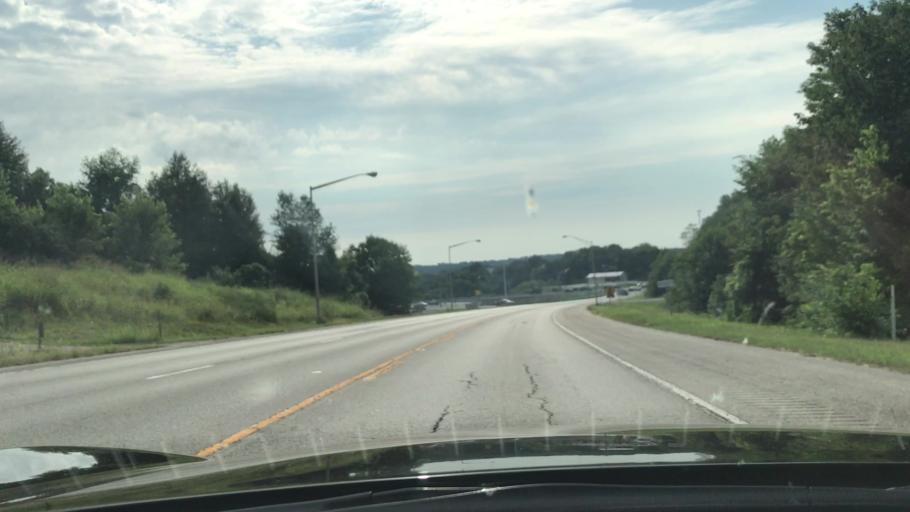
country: US
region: Kentucky
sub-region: Green County
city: Greensburg
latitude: 37.2724
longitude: -85.5003
